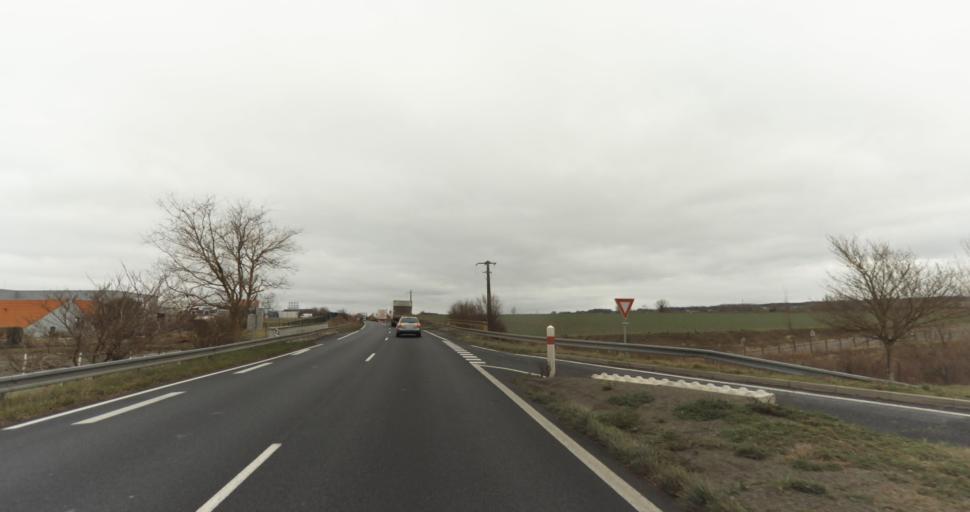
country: FR
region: Pays de la Loire
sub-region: Departement de Maine-et-Loire
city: Doue-la-Fontaine
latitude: 47.1894
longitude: -0.2432
